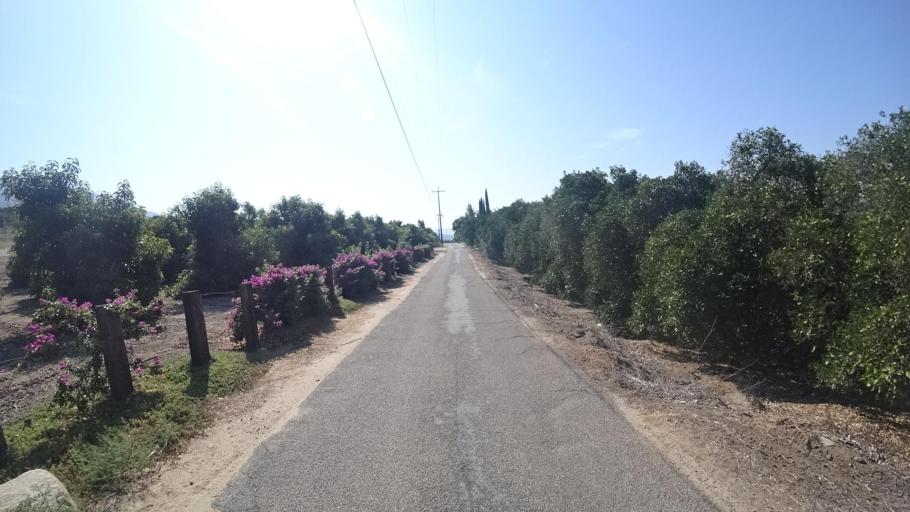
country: US
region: California
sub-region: San Diego County
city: Valley Center
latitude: 33.3367
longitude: -116.9905
